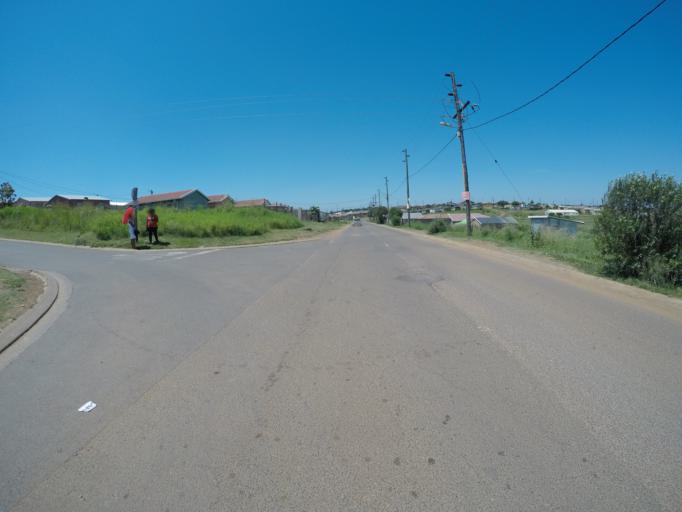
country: ZA
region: KwaZulu-Natal
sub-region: uThungulu District Municipality
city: Empangeni
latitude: -28.7649
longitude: 31.8769
